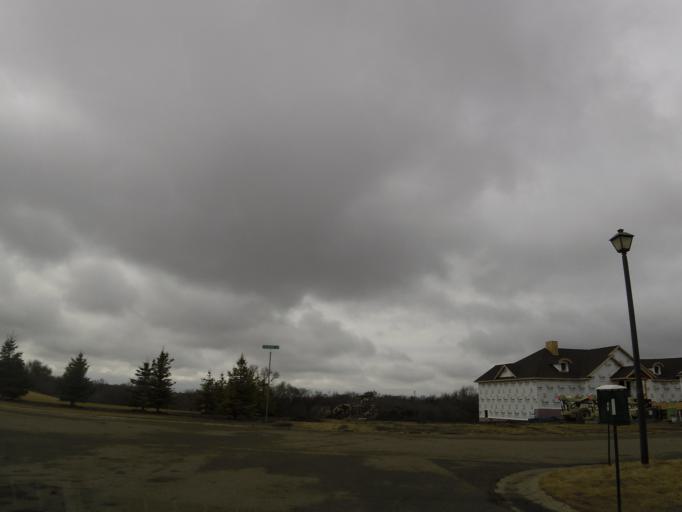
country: US
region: North Dakota
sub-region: Traill County
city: Mayville
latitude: 47.4922
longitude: -97.3135
